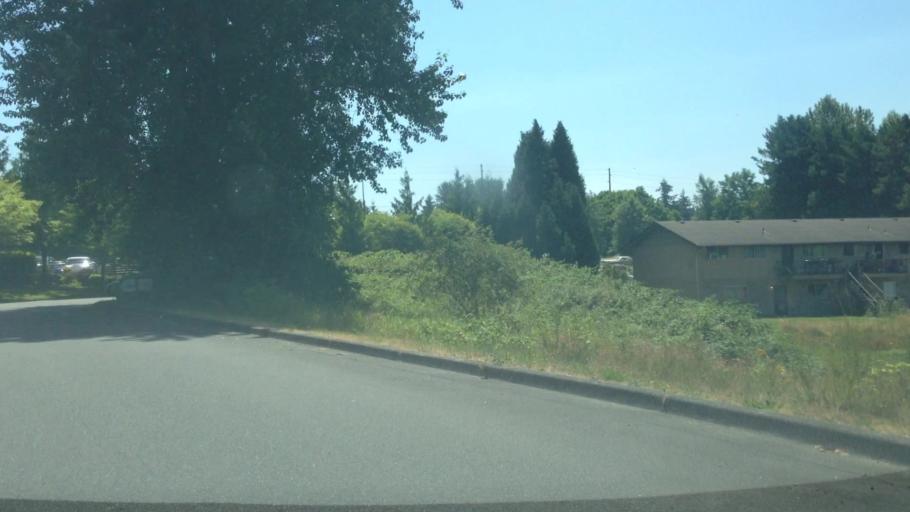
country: US
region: Washington
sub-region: Pierce County
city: Puyallup
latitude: 47.1571
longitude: -122.3094
